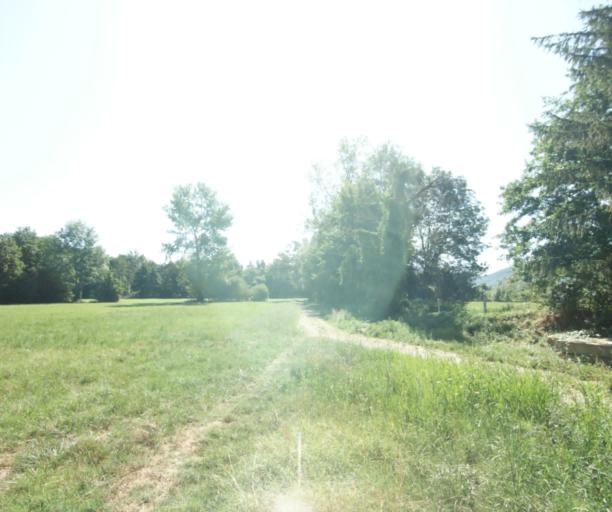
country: FR
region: Midi-Pyrenees
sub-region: Departement du Tarn
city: Soreze
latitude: 43.4577
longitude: 2.0428
